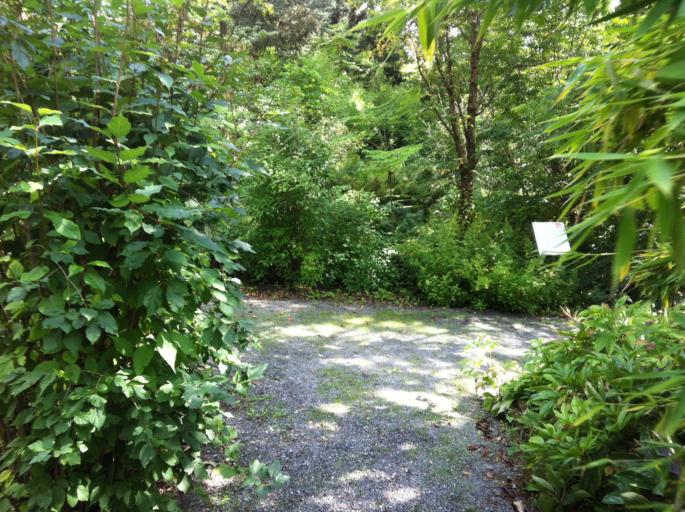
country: DE
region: Bavaria
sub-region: Upper Franconia
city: Bayreuth
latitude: 49.9247
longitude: 11.5866
